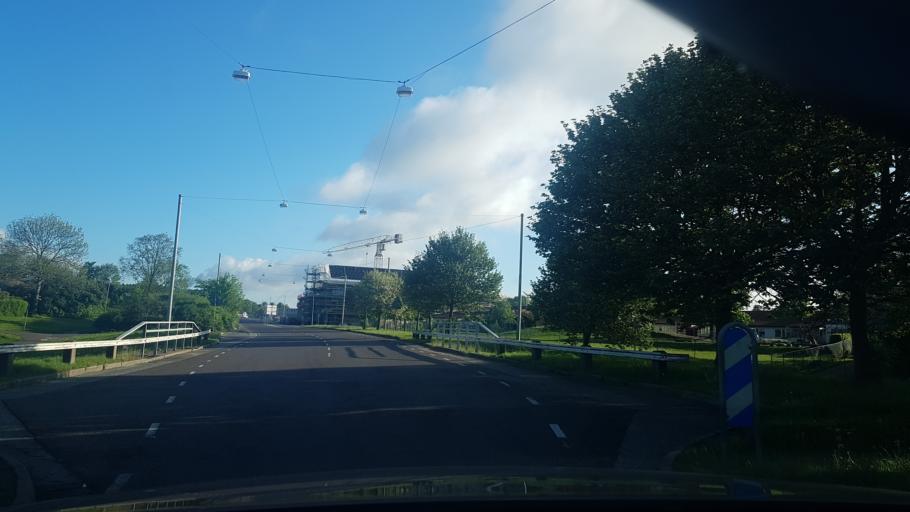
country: SE
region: Vaestra Goetaland
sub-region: Goteborg
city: Majorna
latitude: 57.6392
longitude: 11.8812
